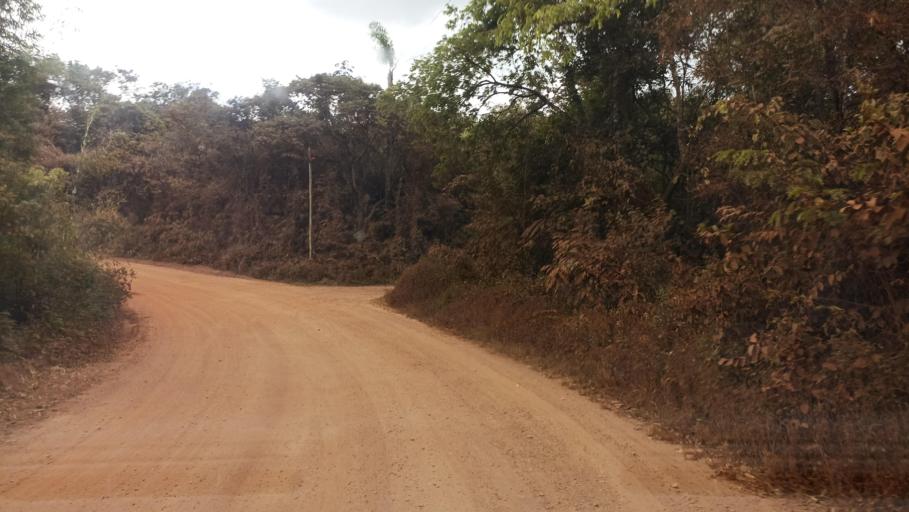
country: BR
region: Minas Gerais
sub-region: Itabirito
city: Itabirito
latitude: -20.3629
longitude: -43.7670
